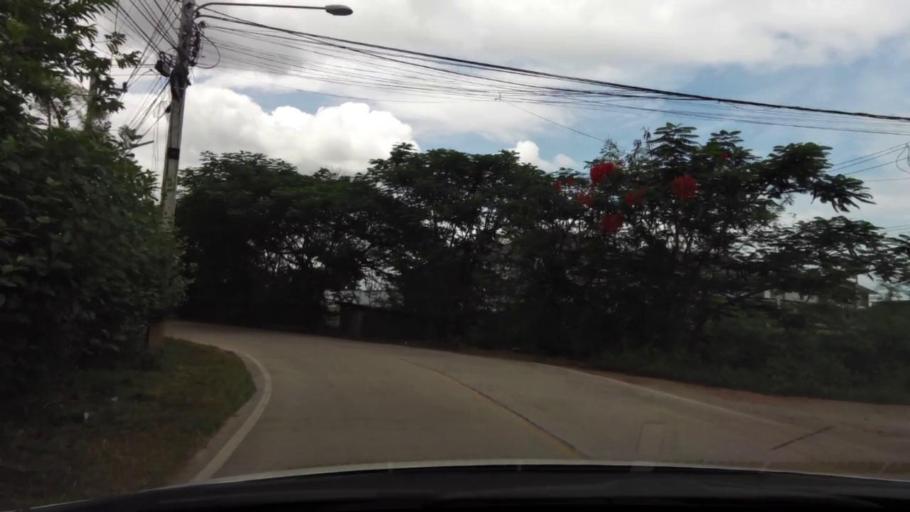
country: TH
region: Ratchaburi
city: Ratchaburi
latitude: 13.5258
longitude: 99.8276
